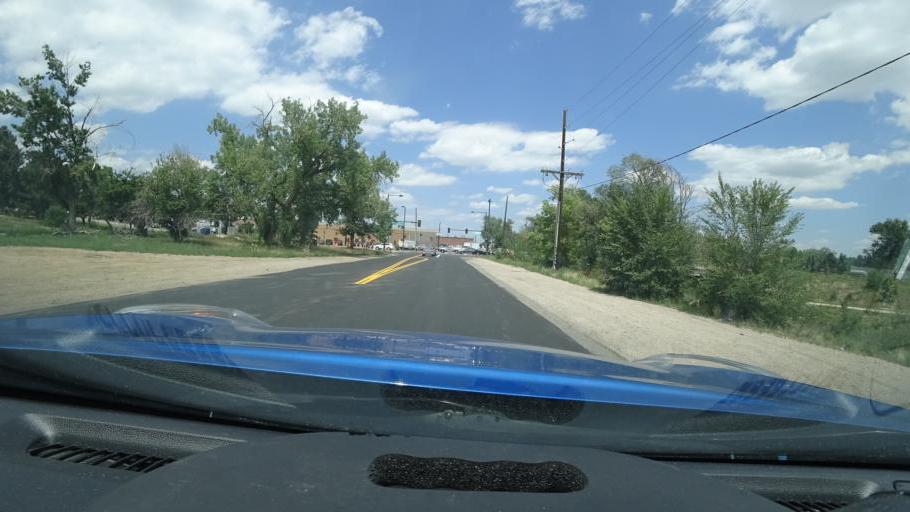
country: US
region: Colorado
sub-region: Arapahoe County
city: Englewood
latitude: 39.6883
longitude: -105.0004
